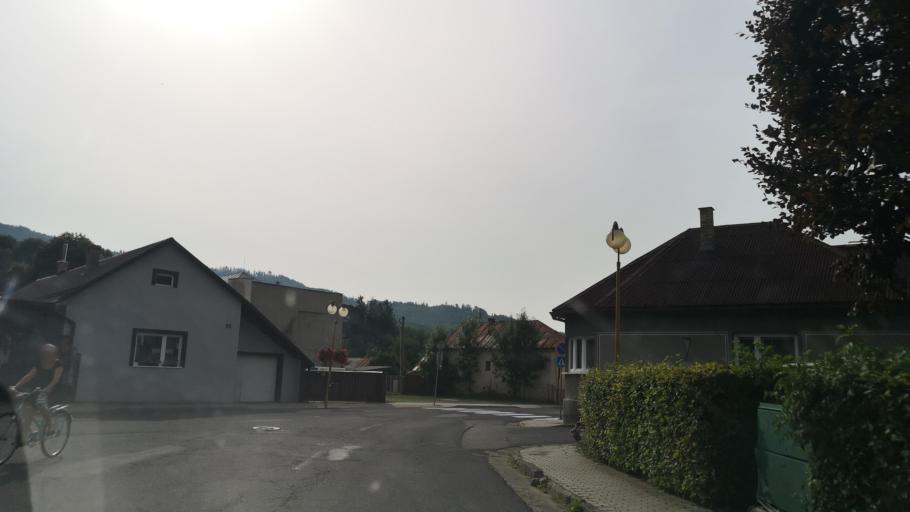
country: SK
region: Banskobystricky
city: Tisovec
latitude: 48.5733
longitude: 19.8401
